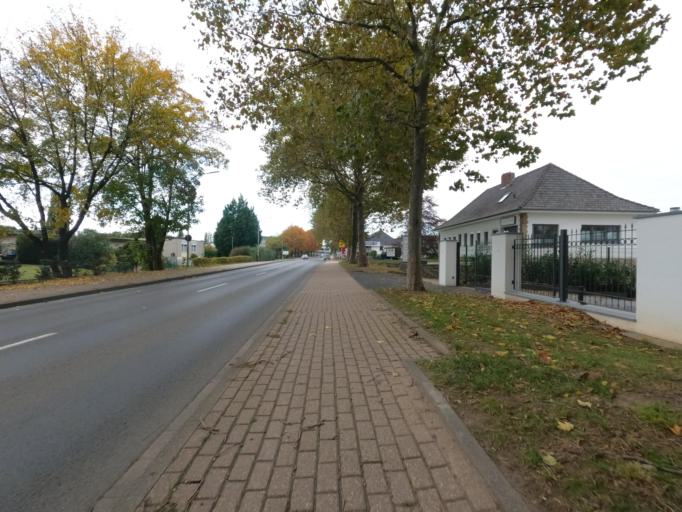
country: DE
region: North Rhine-Westphalia
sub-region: Regierungsbezirk Koln
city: Linnich
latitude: 50.9809
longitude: 6.2794
